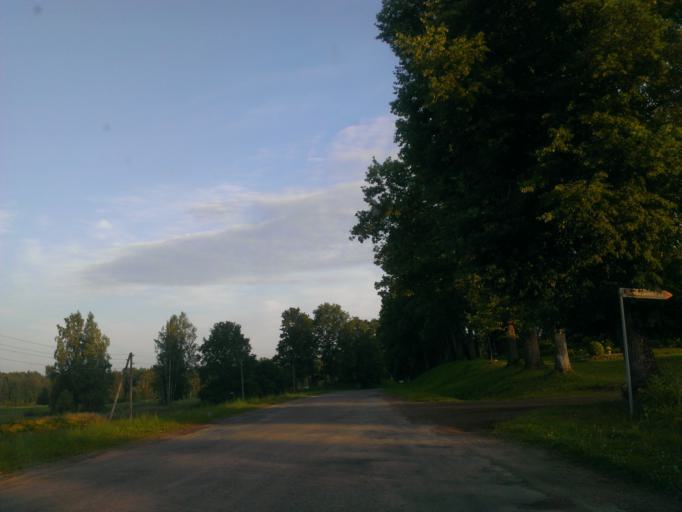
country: LV
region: Amatas Novads
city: Drabesi
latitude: 57.2515
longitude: 25.2789
